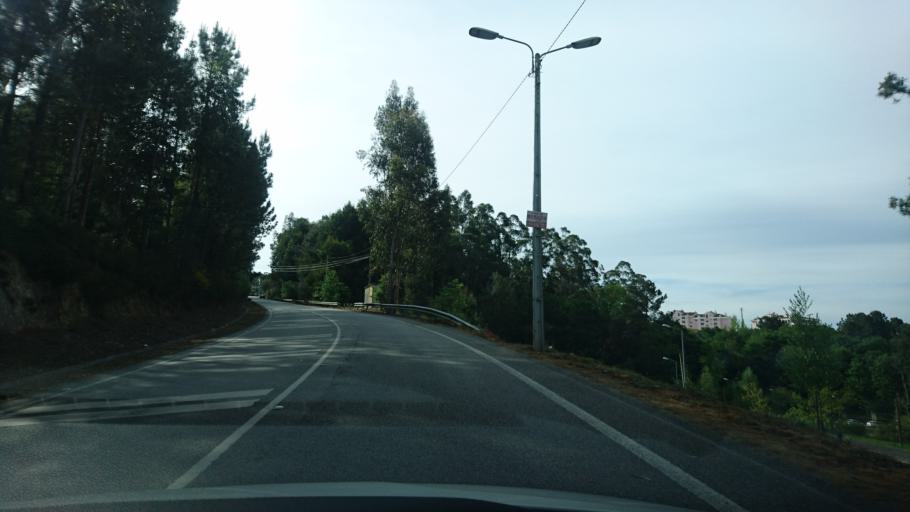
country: PT
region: Aveiro
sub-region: Oliveira de Azemeis
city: Vila Cha
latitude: 40.8630
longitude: -8.4759
